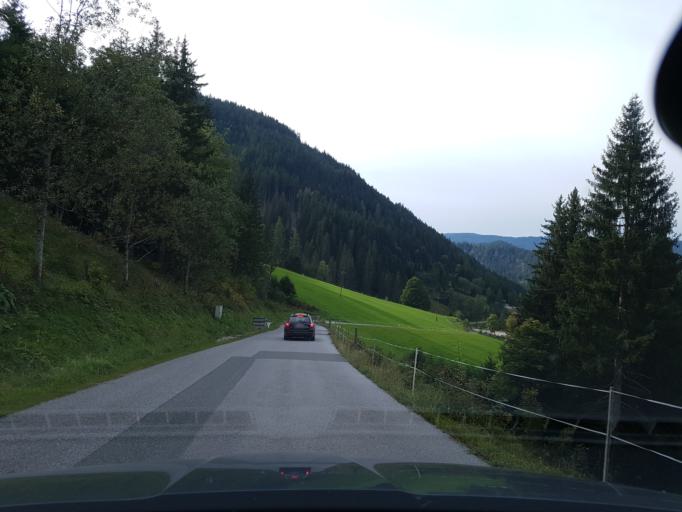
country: AT
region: Salzburg
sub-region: Politischer Bezirk Sankt Johann im Pongau
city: Forstau
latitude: 47.3636
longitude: 13.5589
